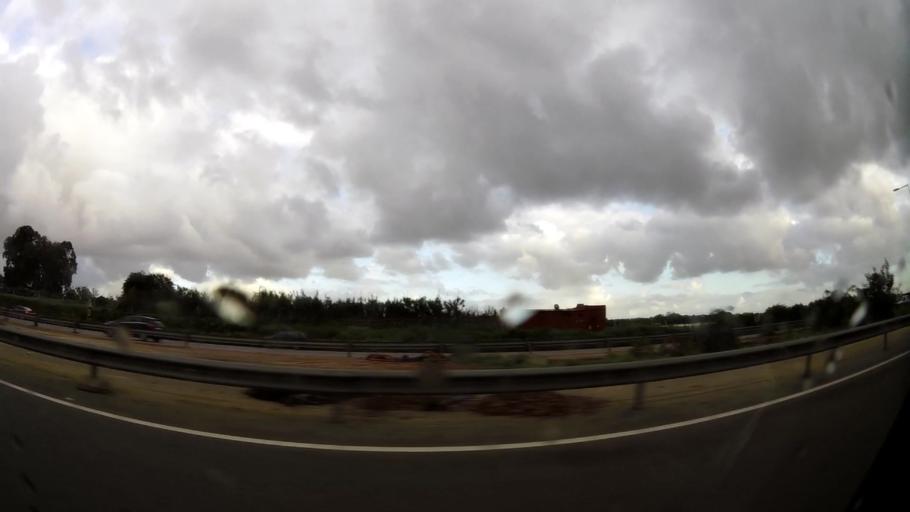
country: MA
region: Grand Casablanca
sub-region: Mohammedia
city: Mohammedia
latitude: 33.6592
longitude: -7.4077
